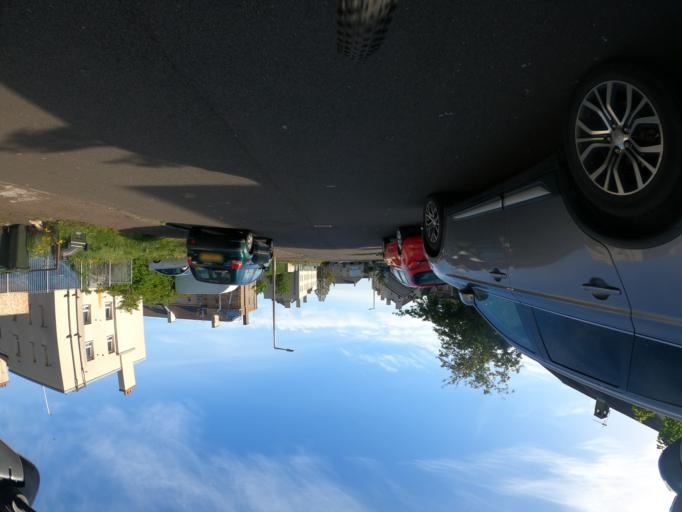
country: GB
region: Scotland
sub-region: Edinburgh
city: Edinburgh
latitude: 55.9773
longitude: -3.2281
